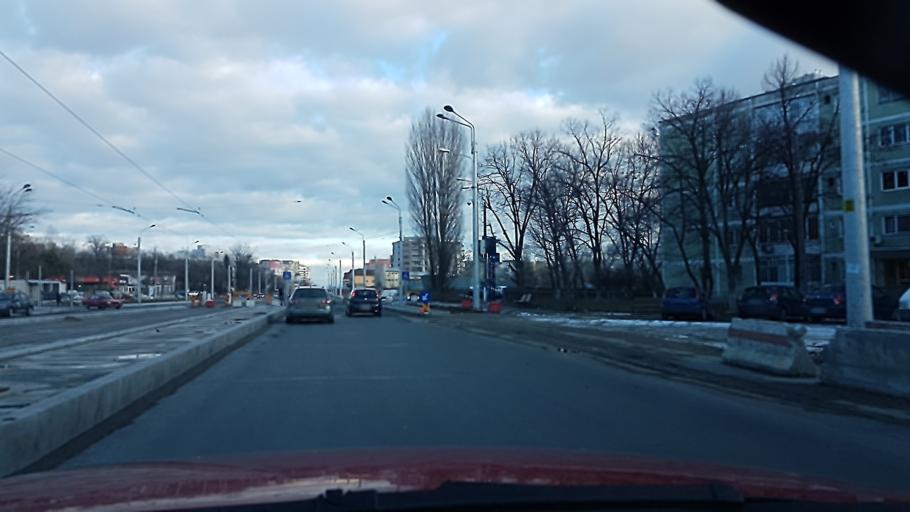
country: RO
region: Ilfov
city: Dobroesti
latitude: 44.4249
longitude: 26.1701
